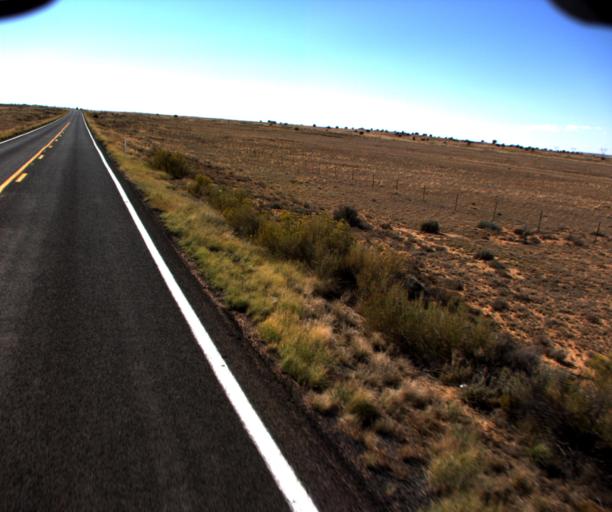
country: US
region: Arizona
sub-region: Coconino County
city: Tuba City
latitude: 35.9667
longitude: -110.8462
